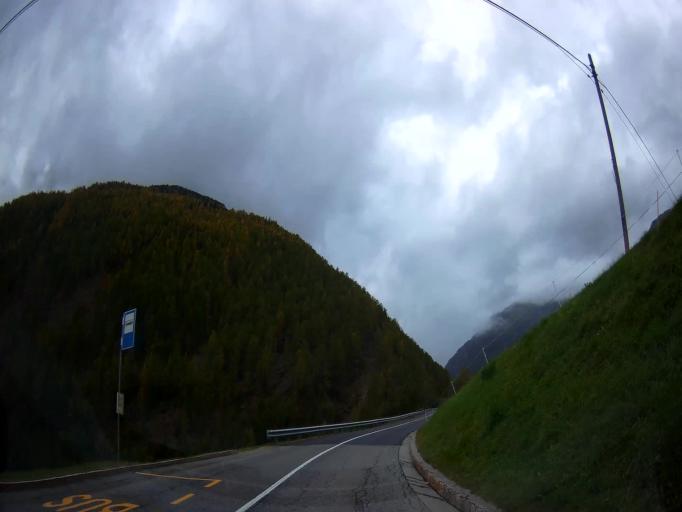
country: IT
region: Trentino-Alto Adige
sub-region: Bolzano
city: Senales
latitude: 46.7290
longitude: 10.8537
